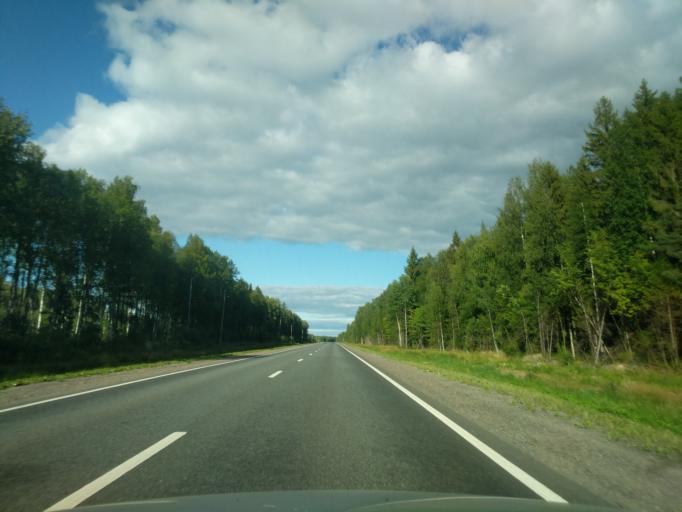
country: RU
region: Kostroma
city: Manturovo
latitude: 58.1548
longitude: 44.3810
